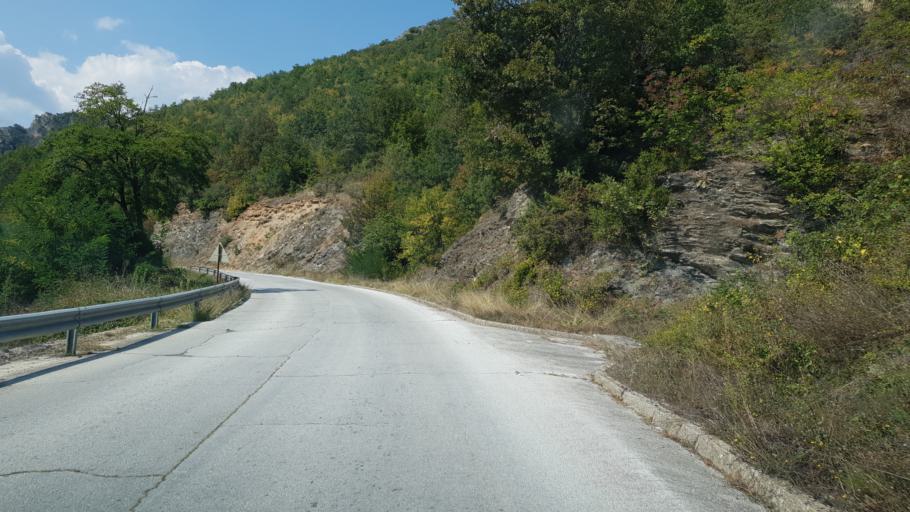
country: MK
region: Makedonski Brod
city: Samokov
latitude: 41.6704
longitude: 21.2410
